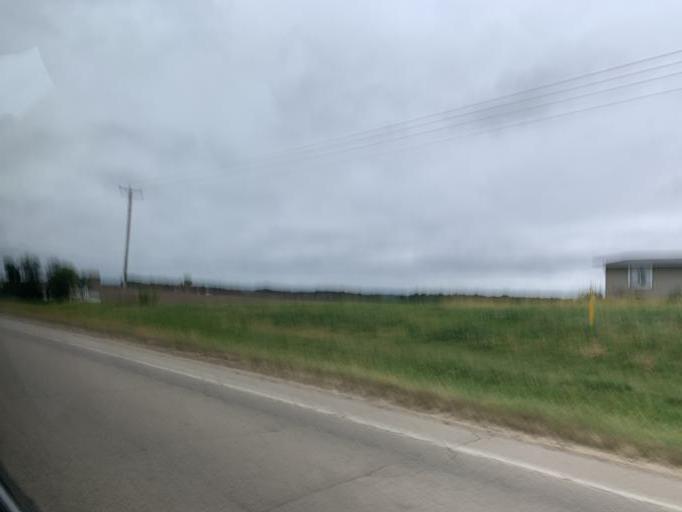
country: US
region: Wisconsin
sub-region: Grant County
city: Muscoda
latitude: 43.2198
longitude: -90.5048
